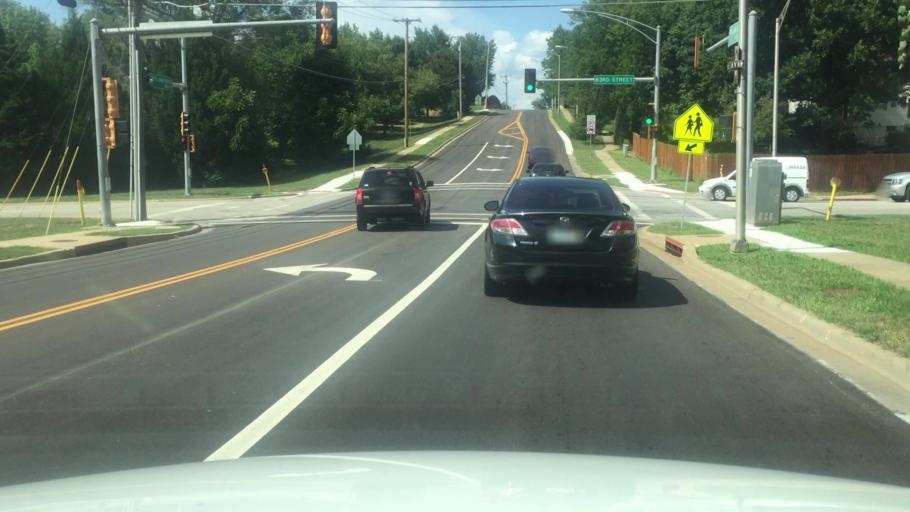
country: US
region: Kansas
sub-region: Johnson County
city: Lenexa
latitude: 38.9780
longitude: -94.7423
